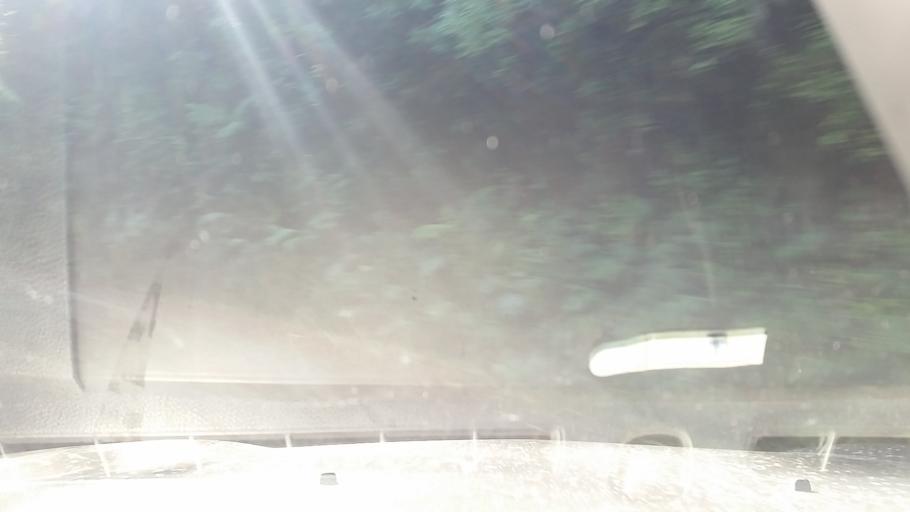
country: NZ
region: Marlborough
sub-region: Marlborough District
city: Picton
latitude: -41.1205
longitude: 173.9902
